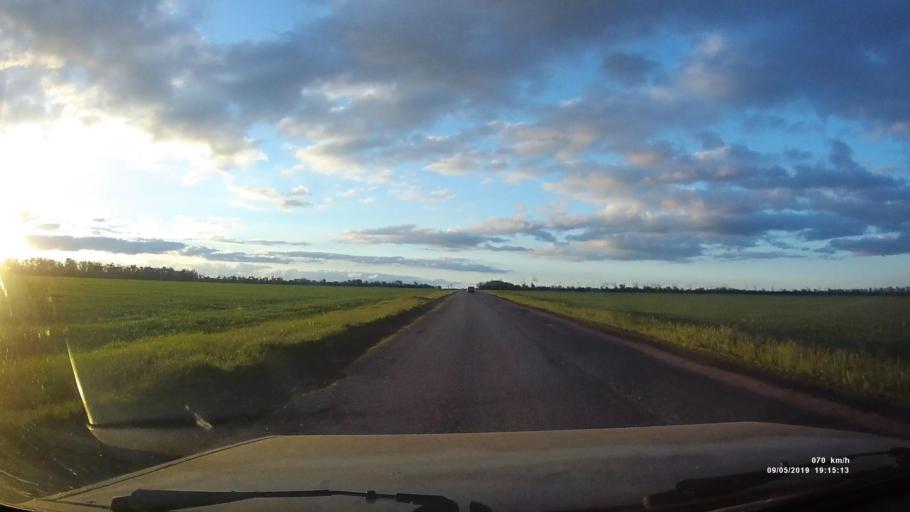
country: RU
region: Krasnodarskiy
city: Kanelovskaya
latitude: 46.7658
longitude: 39.2125
